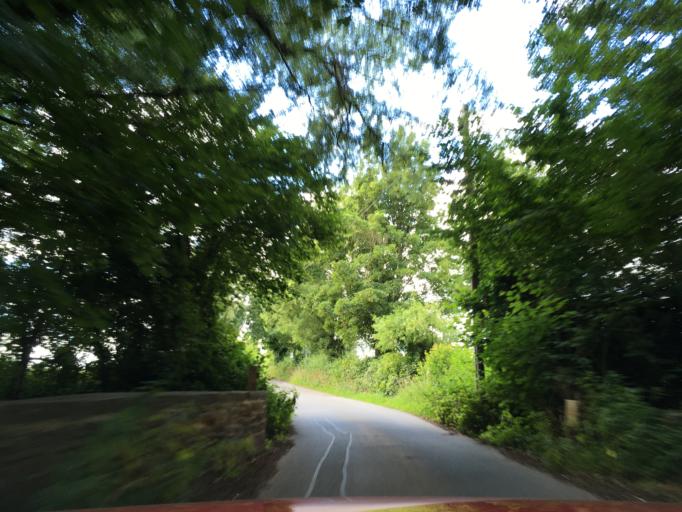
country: GB
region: England
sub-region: Gloucestershire
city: Mitcheldean
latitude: 51.8418
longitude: -2.4264
